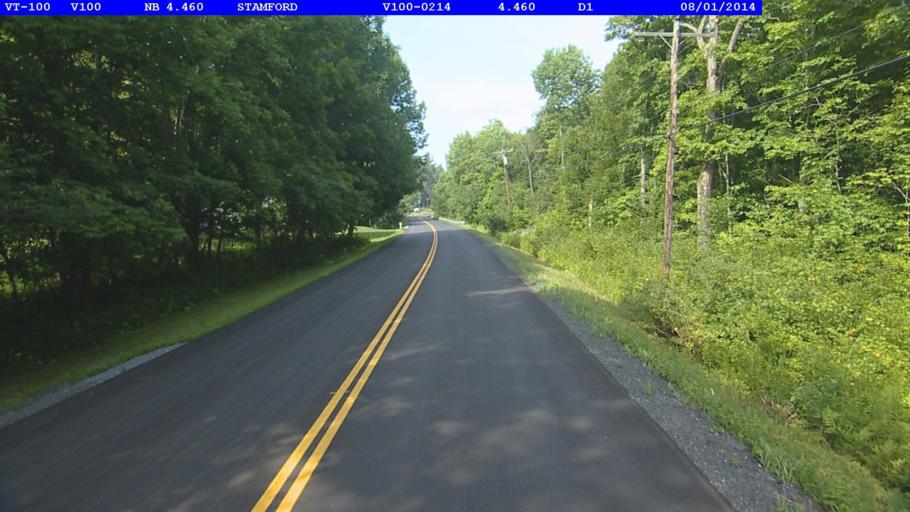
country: US
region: Massachusetts
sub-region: Berkshire County
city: North Adams
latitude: 42.7938
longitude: -73.0294
